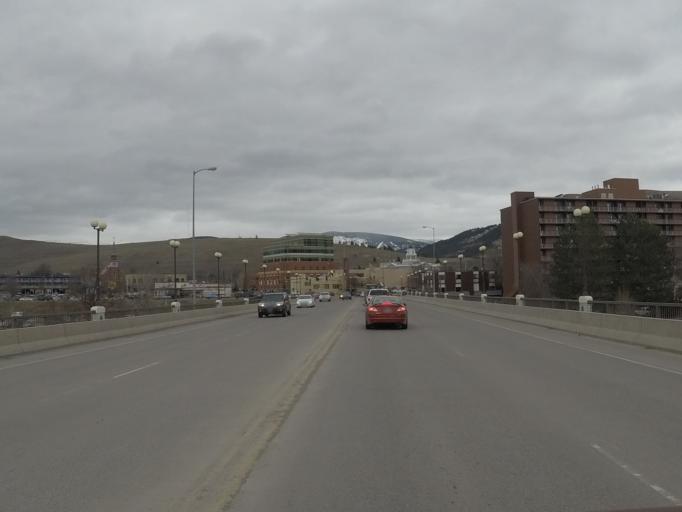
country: US
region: Montana
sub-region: Missoula County
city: Missoula
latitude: 46.8713
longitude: -114.0012
